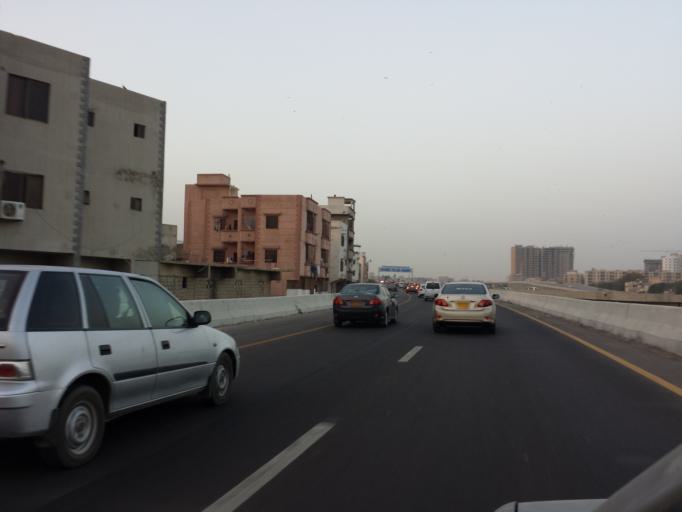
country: PK
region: Sindh
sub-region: Karachi District
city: Karachi
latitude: 24.9014
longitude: 67.0616
